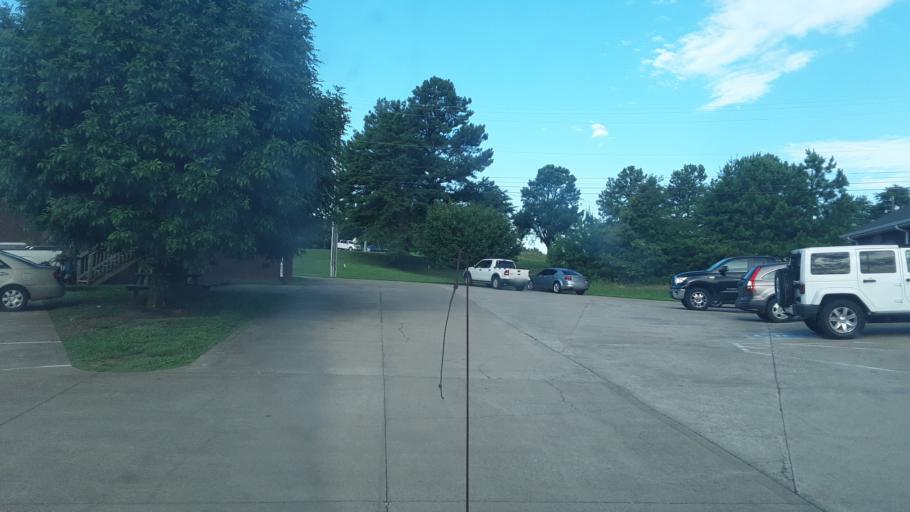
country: US
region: Tennessee
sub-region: Montgomery County
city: Clarksville
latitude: 36.5726
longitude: -87.2947
